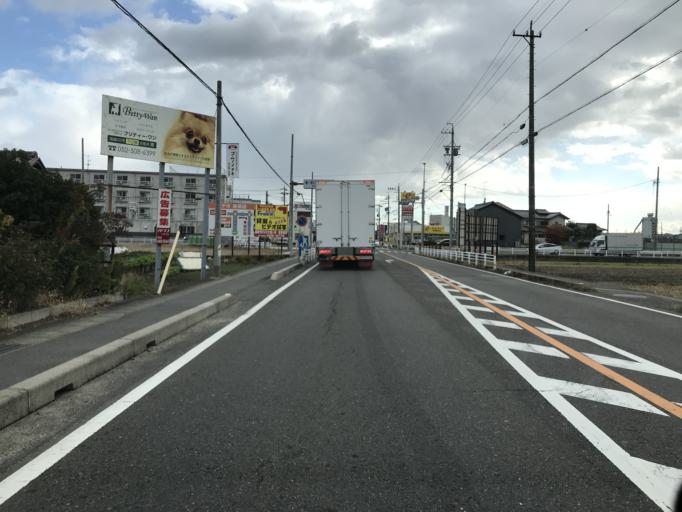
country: JP
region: Aichi
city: Inazawa
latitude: 35.2349
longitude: 136.8352
